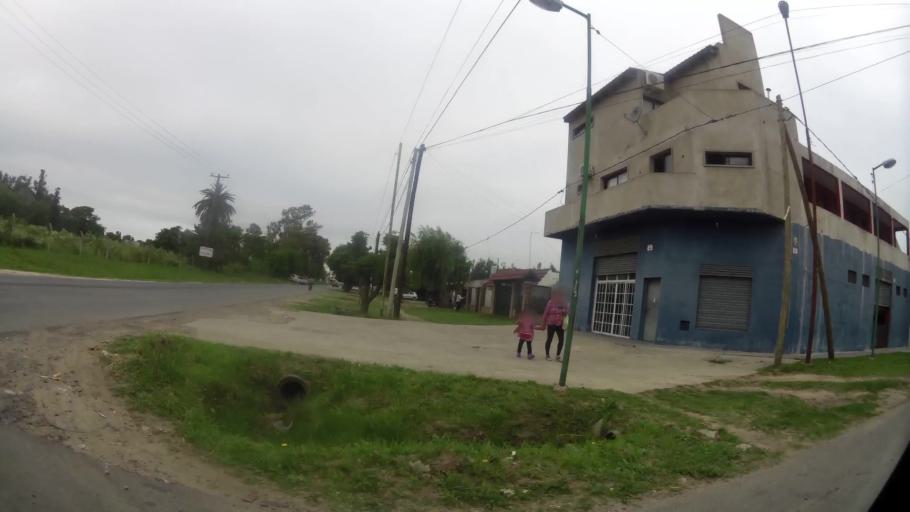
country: AR
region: Buenos Aires
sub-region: Partido de La Plata
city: La Plata
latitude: -34.9361
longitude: -57.9954
